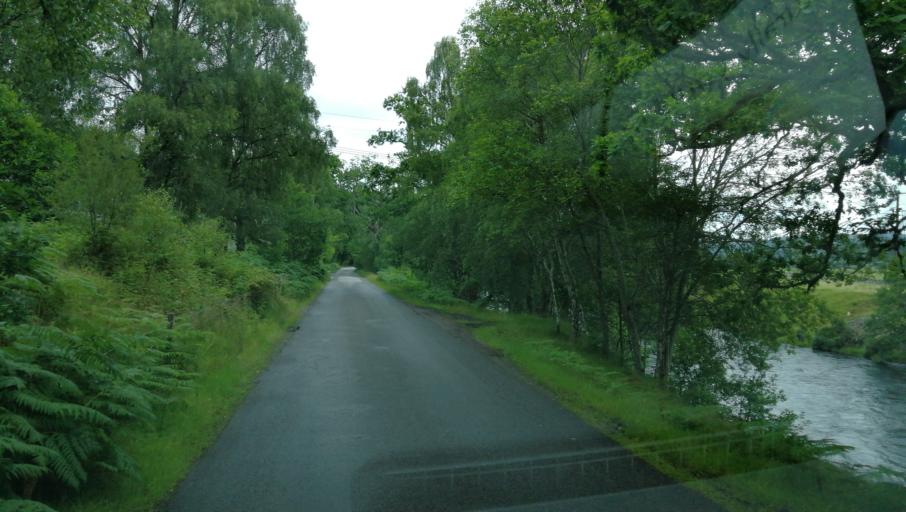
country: GB
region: Scotland
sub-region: Highland
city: Beauly
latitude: 57.3276
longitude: -4.7932
